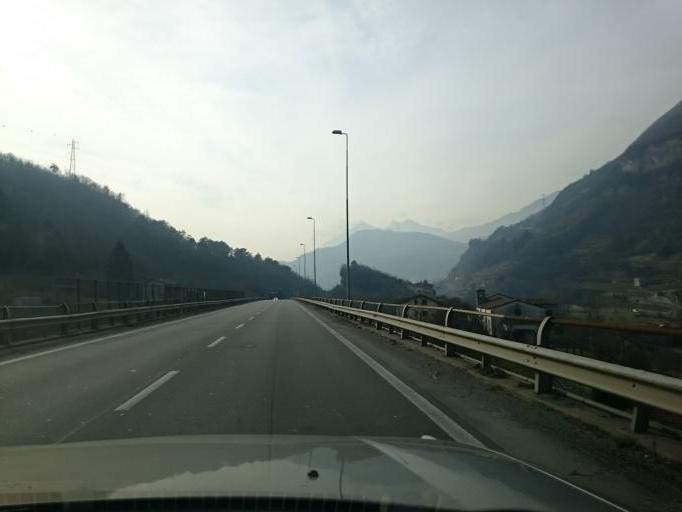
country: IT
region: Lombardy
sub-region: Provincia di Brescia
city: Breno
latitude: 45.9573
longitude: 10.2910
